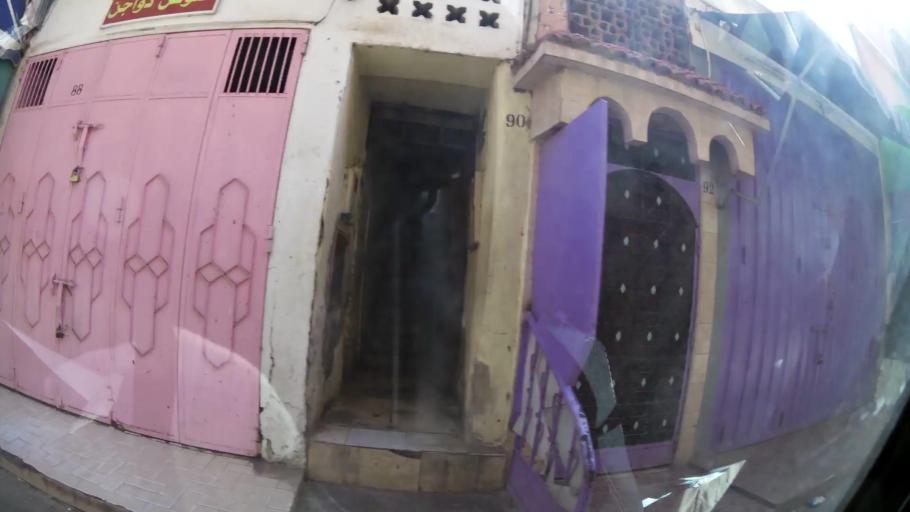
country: MA
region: Souss-Massa-Draa
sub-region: Inezgane-Ait Mellou
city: Inezgane
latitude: 30.3432
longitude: -9.5030
